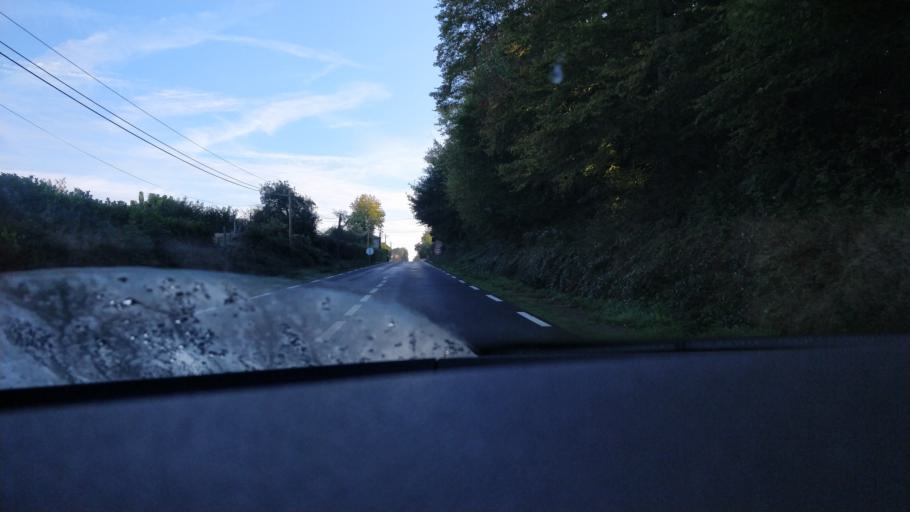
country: FR
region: Limousin
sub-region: Departement de la Haute-Vienne
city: Saint-Leonard-de-Noblat
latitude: 45.8584
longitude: 1.5114
